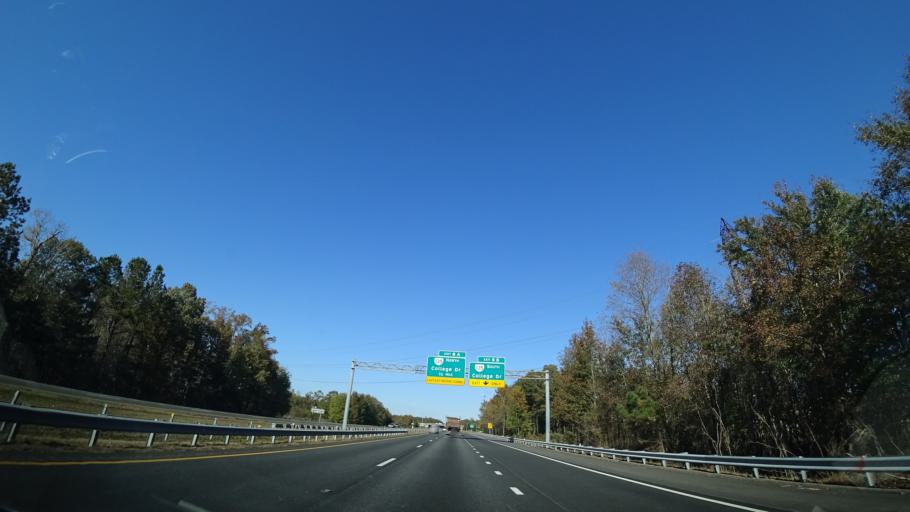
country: US
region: Virginia
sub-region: City of Portsmouth
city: Portsmouth Heights
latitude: 36.8814
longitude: -76.4314
